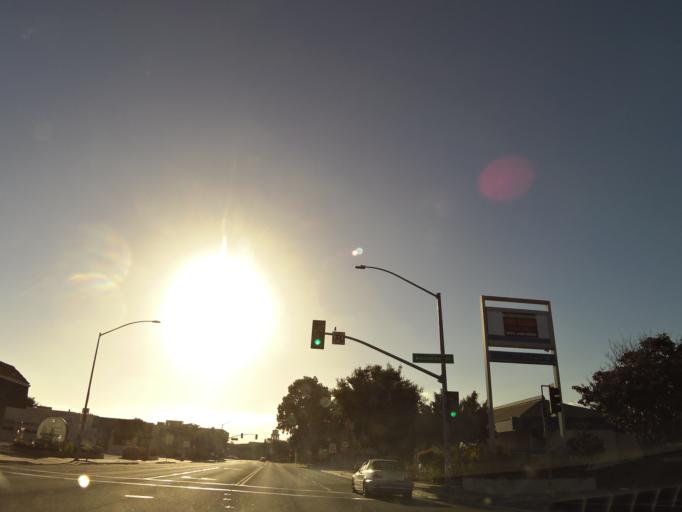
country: US
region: California
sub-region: Monterey County
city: Salinas
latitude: 36.6708
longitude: -121.6531
